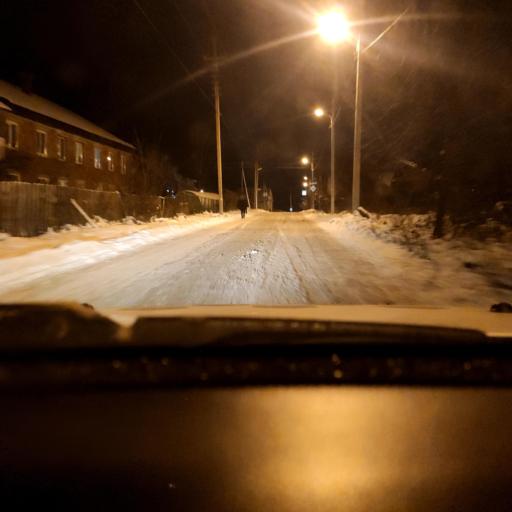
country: RU
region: Perm
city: Ferma
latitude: 57.9592
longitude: 56.3736
